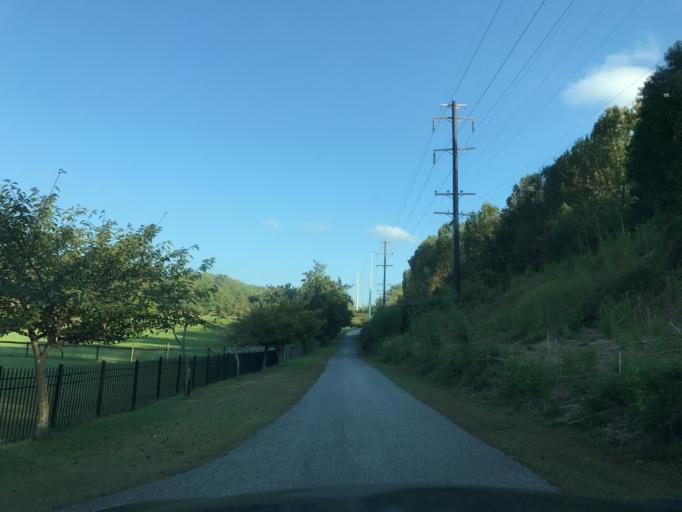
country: US
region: Maryland
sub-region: Anne Arundel County
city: Crownsville
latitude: 39.0490
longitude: -76.6268
